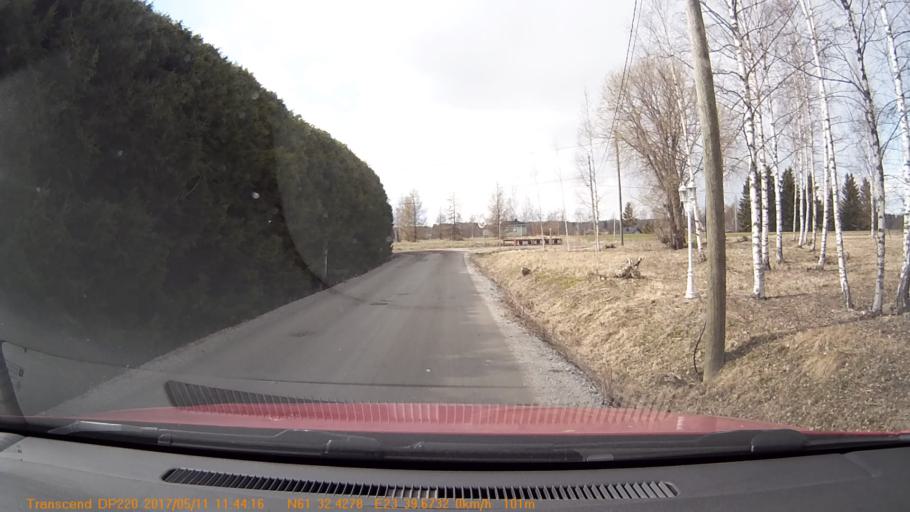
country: FI
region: Pirkanmaa
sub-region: Tampere
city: Yloejaervi
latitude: 61.5405
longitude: 23.6613
